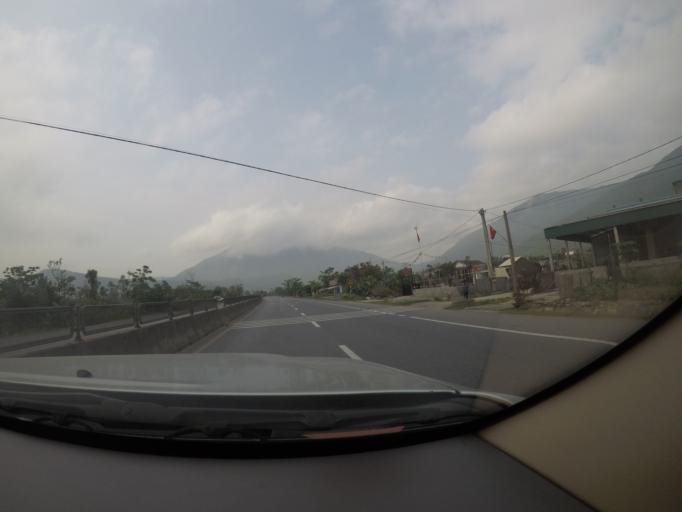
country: VN
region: Ha Tinh
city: Ky Anh
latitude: 17.9746
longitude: 106.4728
